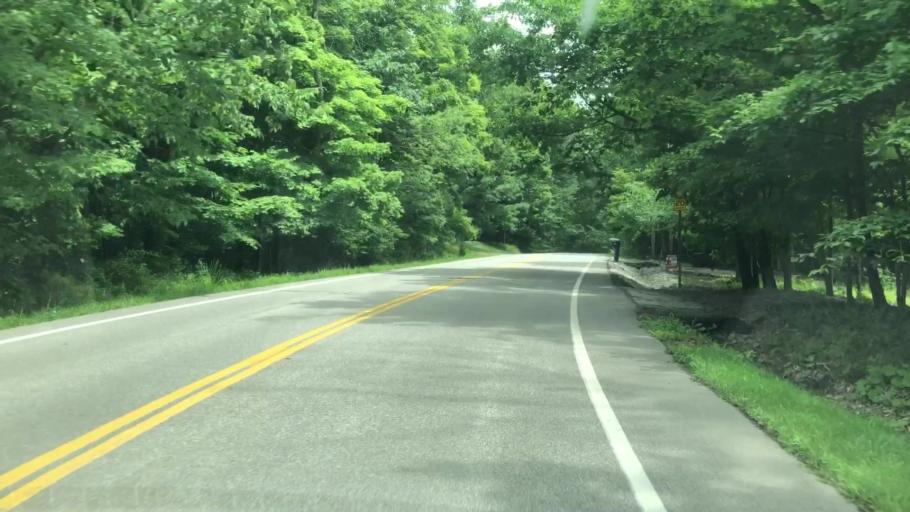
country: US
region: Ohio
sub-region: Summit County
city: Montrose-Ghent
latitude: 41.1696
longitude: -81.6123
